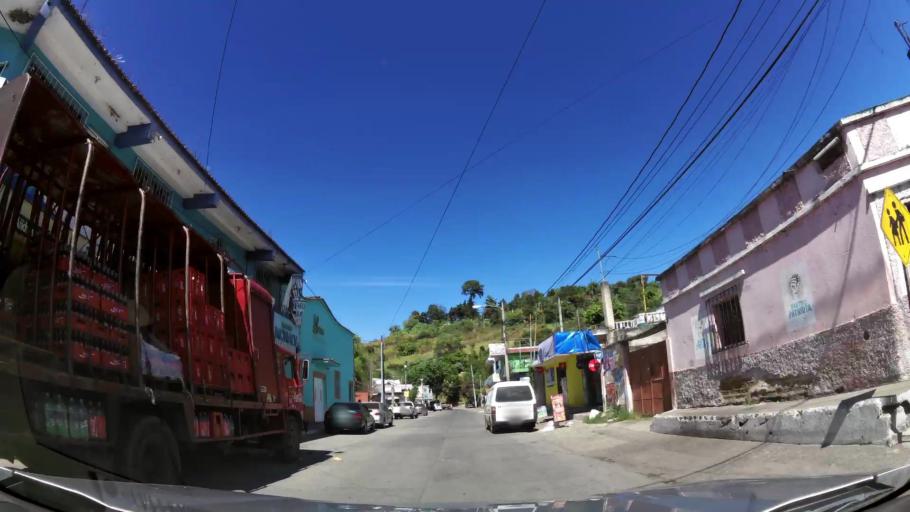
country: GT
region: Guatemala
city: Villa Canales
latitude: 14.4854
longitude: -90.5334
